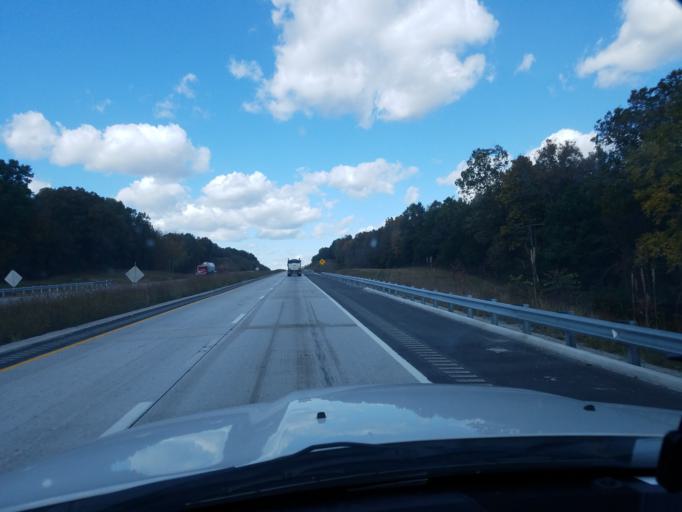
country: US
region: Kentucky
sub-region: Ohio County
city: Oak Grove
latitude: 37.3201
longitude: -86.7442
